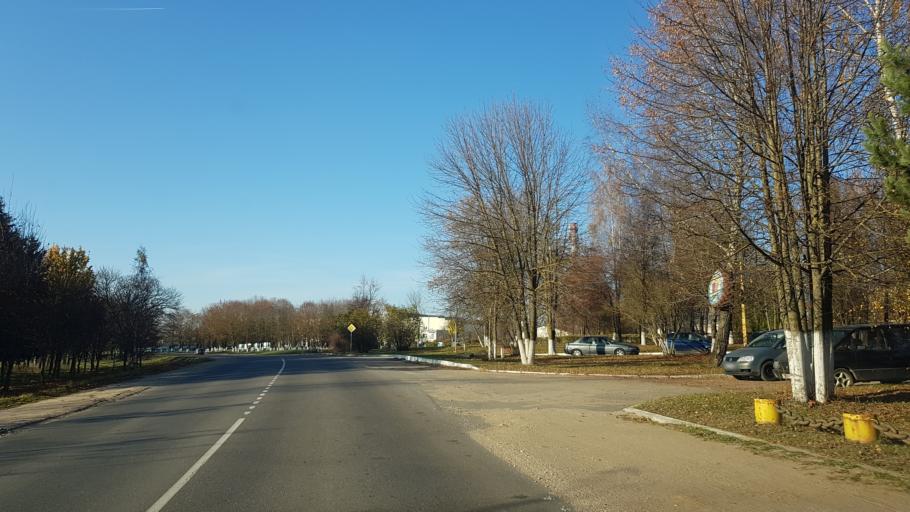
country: BY
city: Fanipol
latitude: 53.7334
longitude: 27.3309
